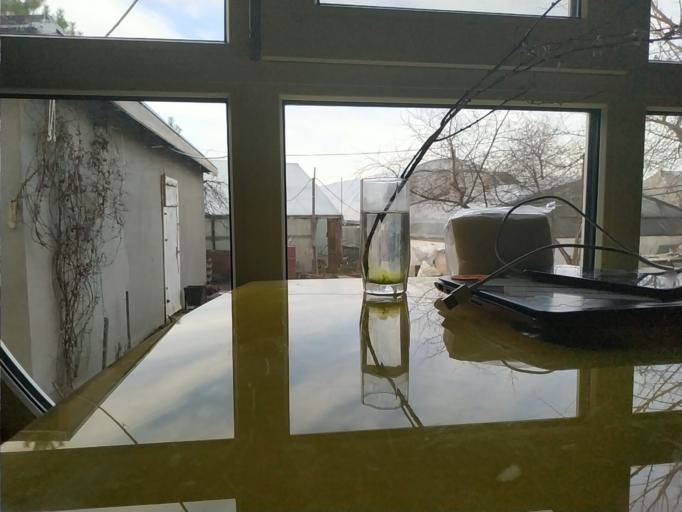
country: RU
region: Republic of Karelia
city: Suoyarvi
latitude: 61.8857
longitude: 32.2619
